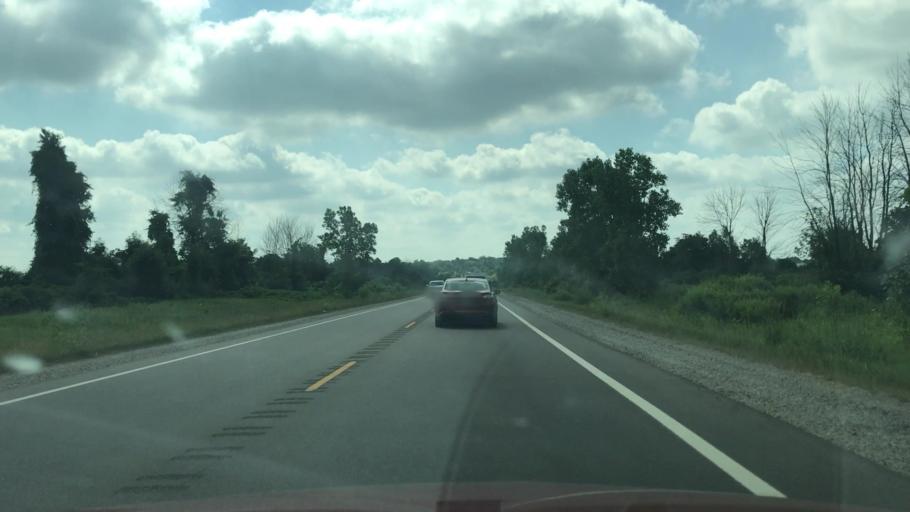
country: US
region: Michigan
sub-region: Kent County
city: Kent City
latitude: 43.2048
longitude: -85.7371
